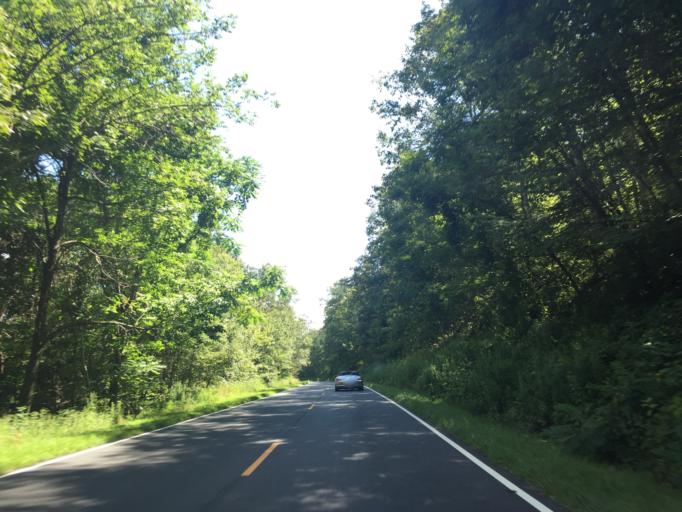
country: US
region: Virginia
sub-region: Page County
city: Luray
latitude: 38.7338
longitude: -78.3182
